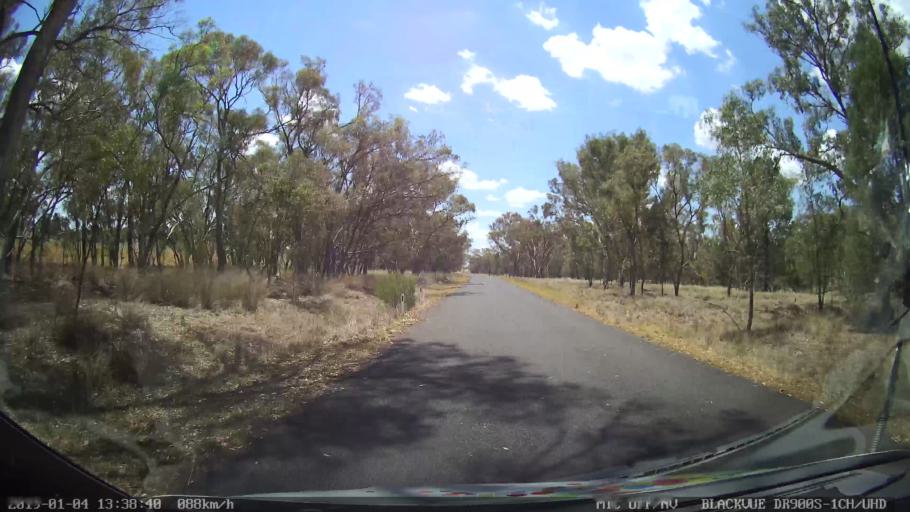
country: AU
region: New South Wales
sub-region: Dubbo Municipality
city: Dubbo
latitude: -32.5352
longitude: 148.5489
